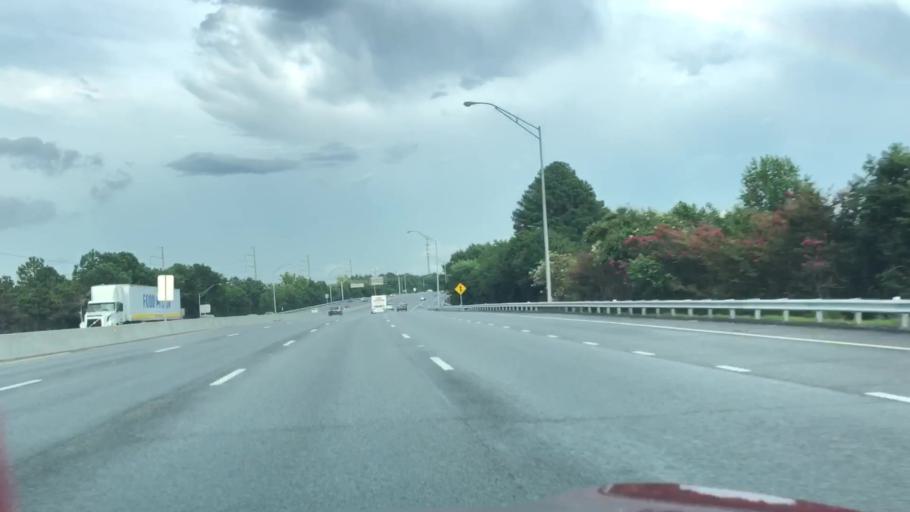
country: US
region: Virginia
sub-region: City of Virginia Beach
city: Virginia Beach
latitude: 36.8389
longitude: -76.0968
